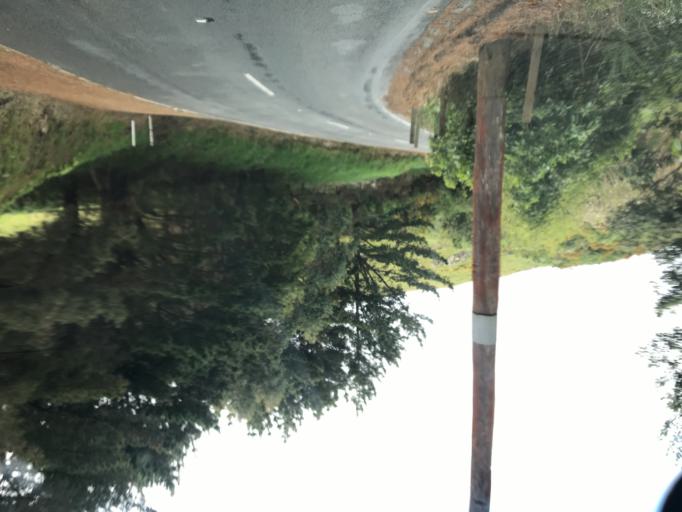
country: NZ
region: Wellington
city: Petone
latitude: -41.2132
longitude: 174.7963
